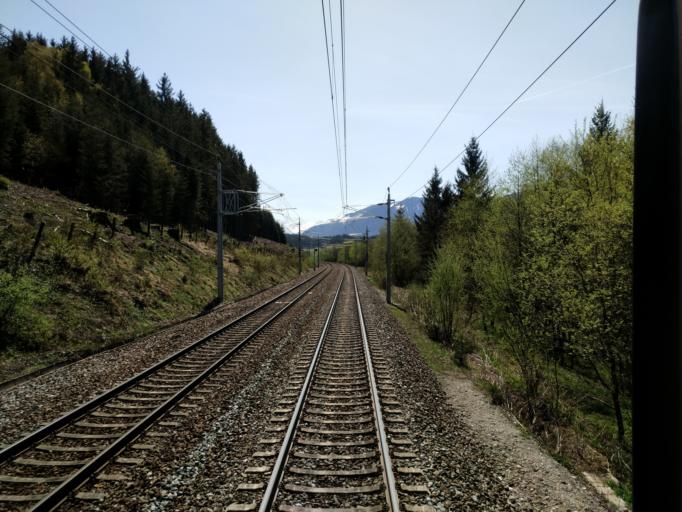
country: AT
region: Salzburg
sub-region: Politischer Bezirk Zell am See
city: Saalfelden am Steinernen Meer
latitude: 47.4155
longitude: 12.8288
